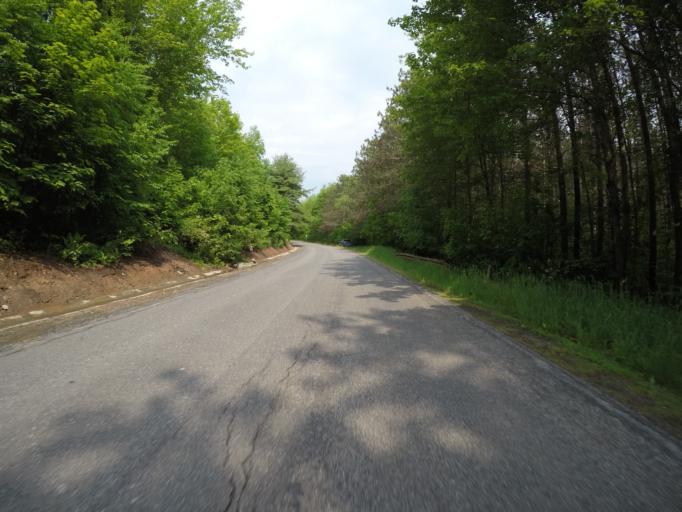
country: US
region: New York
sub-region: Sullivan County
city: Livingston Manor
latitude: 42.0832
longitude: -74.7968
